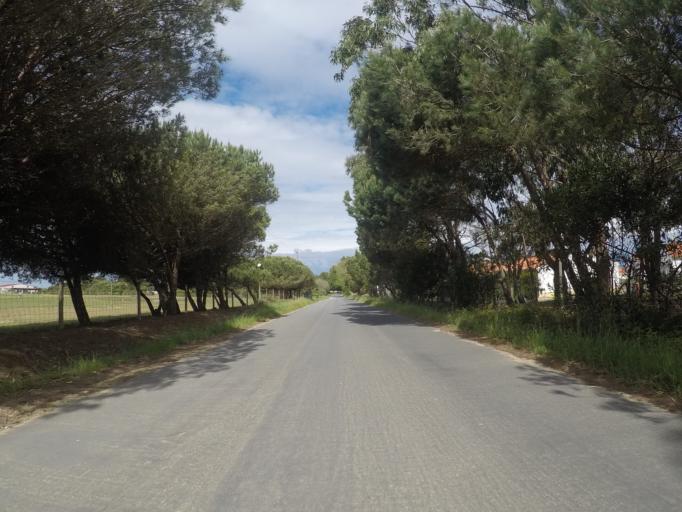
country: PT
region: Beja
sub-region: Odemira
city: Sao Teotonio
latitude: 37.4947
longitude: -8.7858
